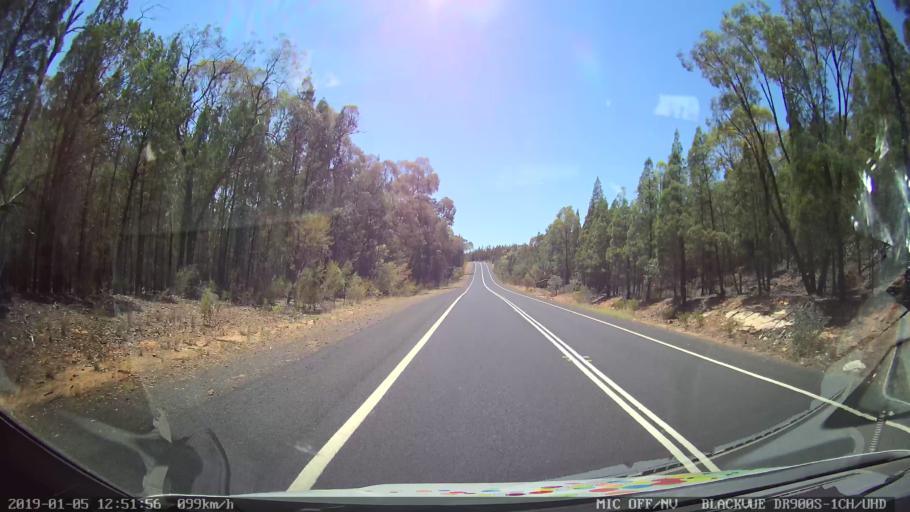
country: AU
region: New South Wales
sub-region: Warrumbungle Shire
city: Coonabarabran
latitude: -31.1216
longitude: 149.6481
